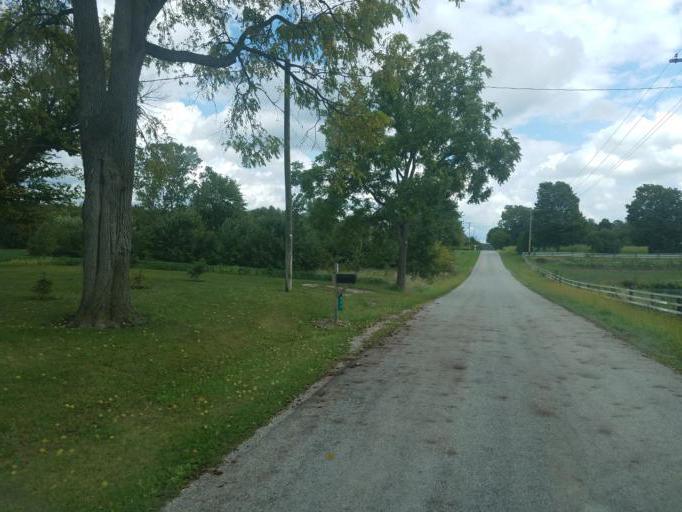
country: US
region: Ohio
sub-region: Huron County
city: Plymouth
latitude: 41.0453
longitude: -82.6153
